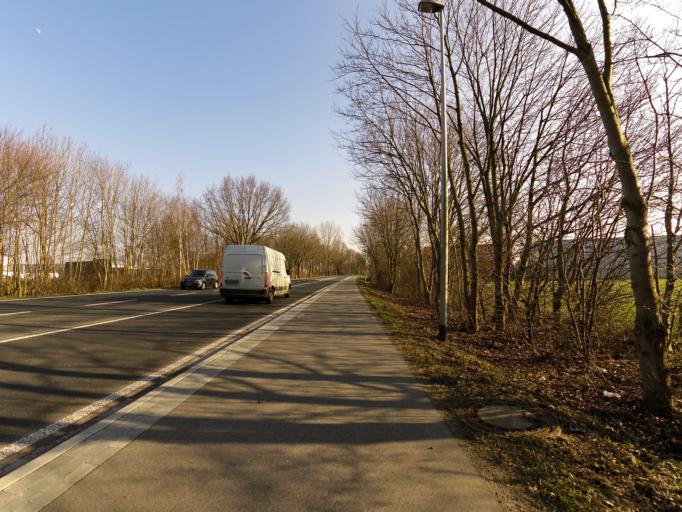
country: DE
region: North Rhine-Westphalia
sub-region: Regierungsbezirk Dusseldorf
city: Emmerich
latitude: 51.8417
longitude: 6.2743
